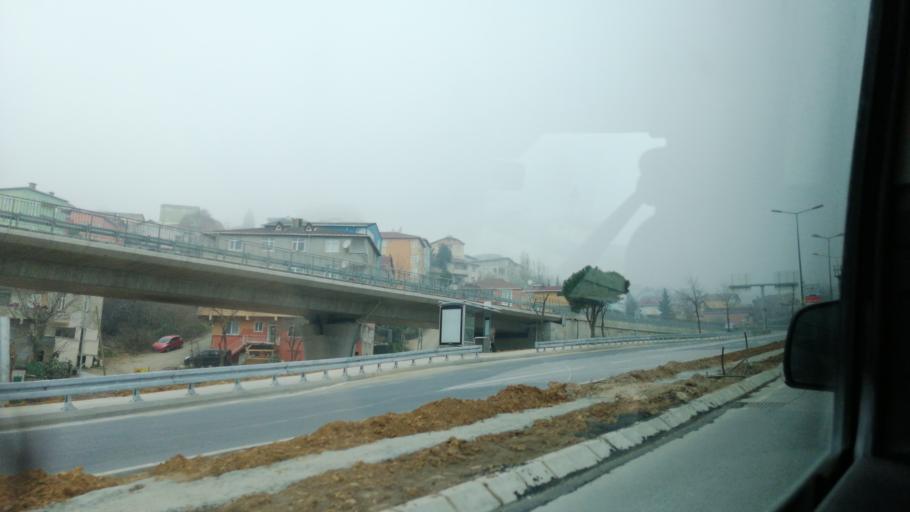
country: TR
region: Istanbul
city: Umraniye
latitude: 41.0856
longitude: 29.0859
